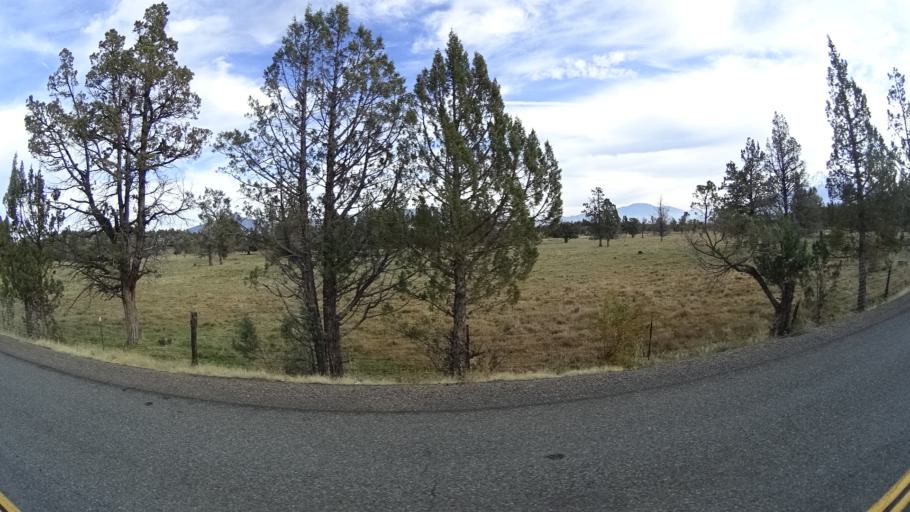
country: US
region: California
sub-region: Siskiyou County
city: Montague
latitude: 41.6353
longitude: -122.4383
